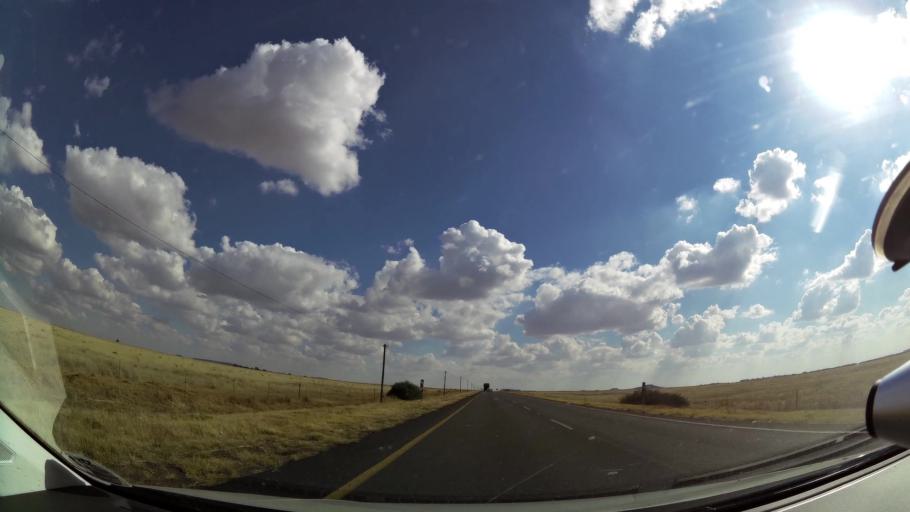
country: ZA
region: Orange Free State
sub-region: Mangaung Metropolitan Municipality
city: Bloemfontein
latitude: -29.1544
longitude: 25.7247
